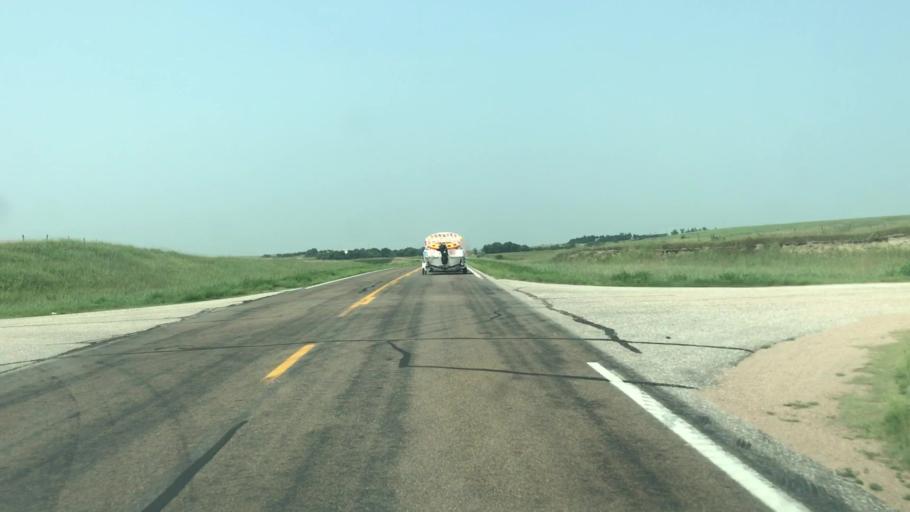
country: US
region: Nebraska
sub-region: Sherman County
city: Loup City
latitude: 41.2505
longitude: -98.9391
